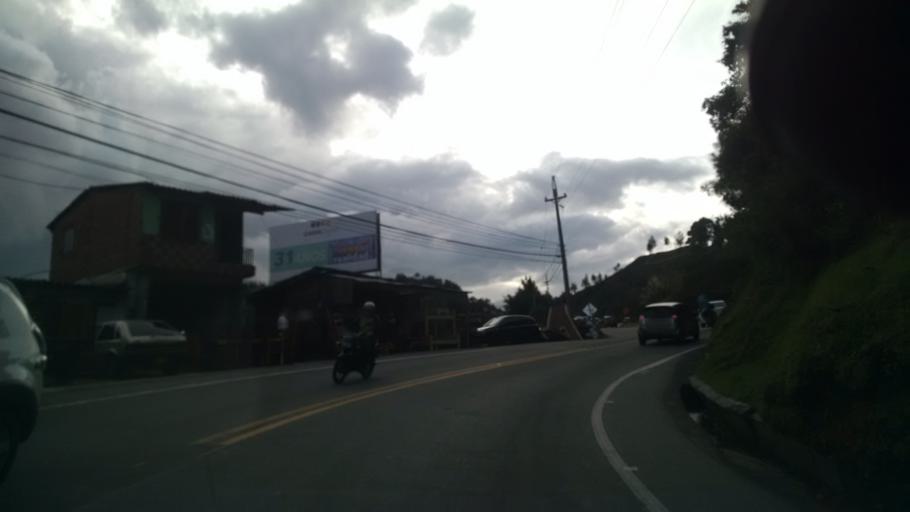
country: CO
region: Antioquia
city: El Retiro
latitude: 6.1386
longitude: -75.5118
